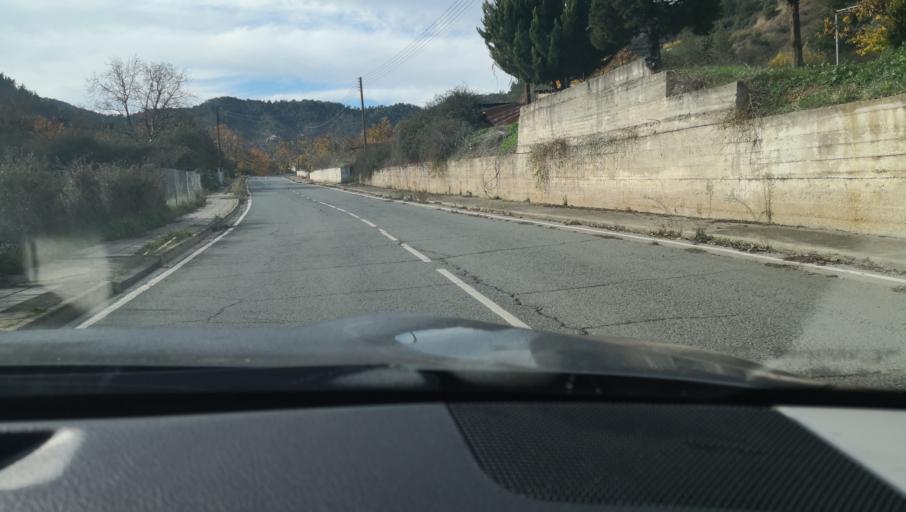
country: CY
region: Lefkosia
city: Lefka
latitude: 35.0336
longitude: 32.7315
